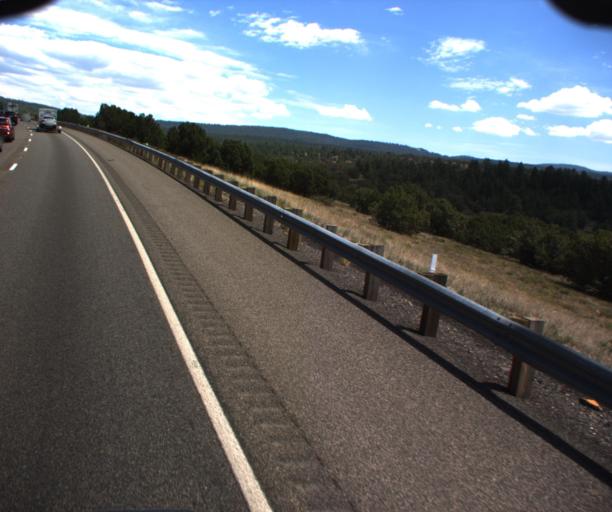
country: US
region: Arizona
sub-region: Yavapai County
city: Village of Oak Creek (Big Park)
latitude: 34.7899
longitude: -111.5912
